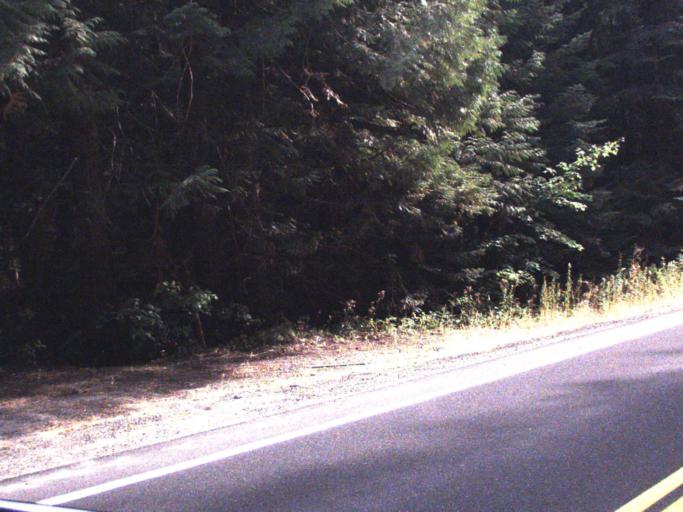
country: US
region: Washington
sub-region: Spokane County
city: Otis Orchards-East Farms
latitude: 47.8744
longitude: -117.1523
